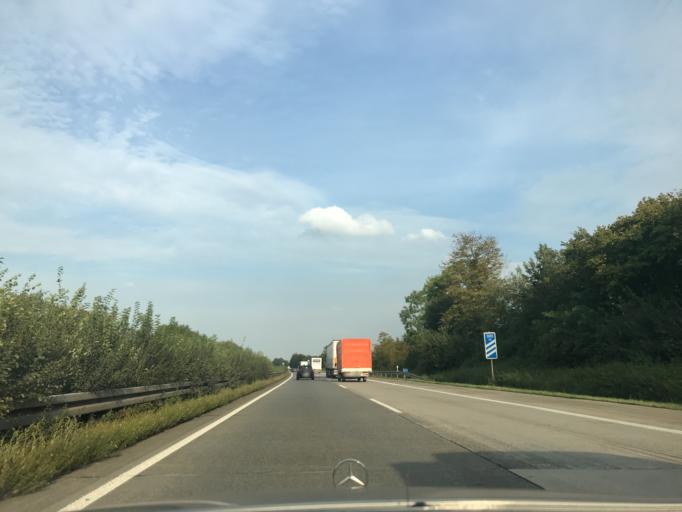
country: DE
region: North Rhine-Westphalia
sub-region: Regierungsbezirk Arnsberg
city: Soest
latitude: 51.5457
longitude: 8.1231
